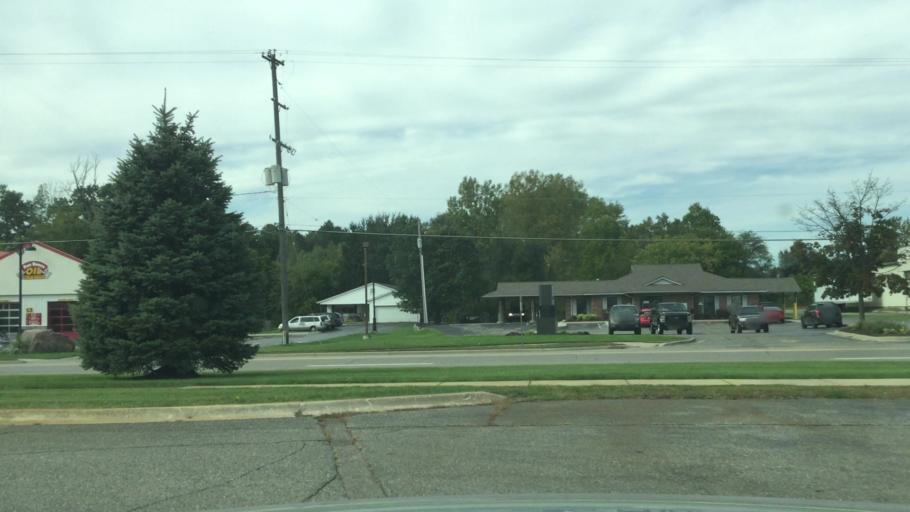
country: US
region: Michigan
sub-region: Oakland County
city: Holly
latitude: 42.8091
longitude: -83.6278
